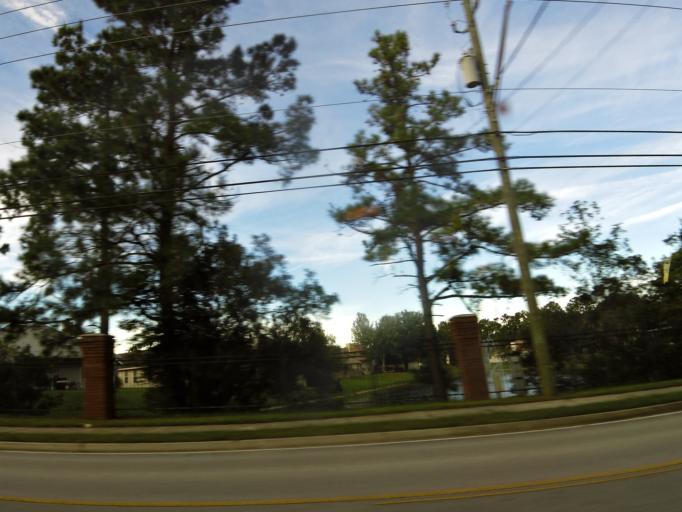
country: US
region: Florida
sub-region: Saint Johns County
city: Fruit Cove
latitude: 30.1617
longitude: -81.5631
